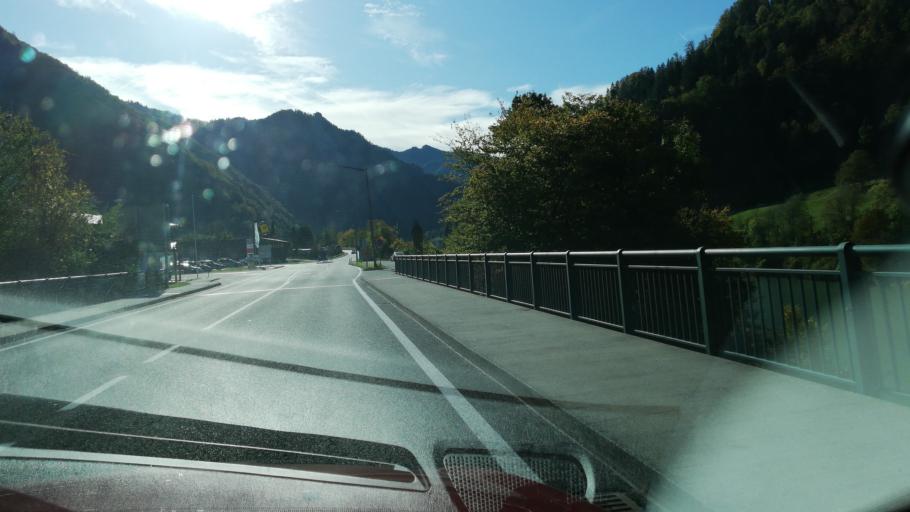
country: AT
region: Upper Austria
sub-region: Politischer Bezirk Steyr-Land
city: Losenstein
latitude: 47.9214
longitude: 14.4386
